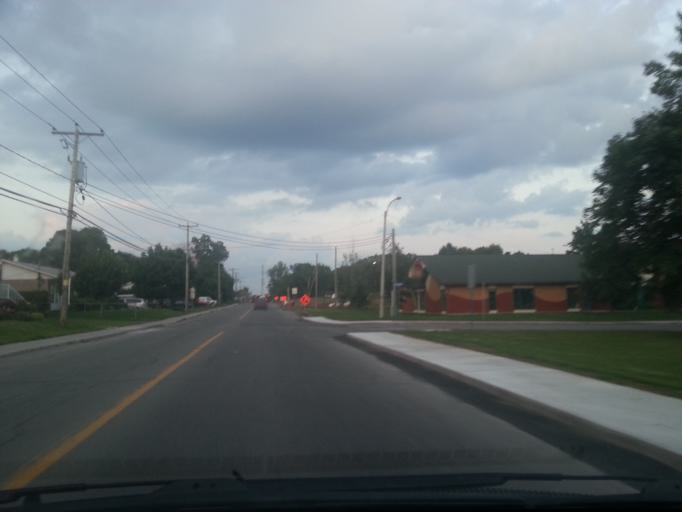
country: CA
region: Quebec
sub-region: Outaouais
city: Gatineau
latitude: 45.4926
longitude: -75.6462
